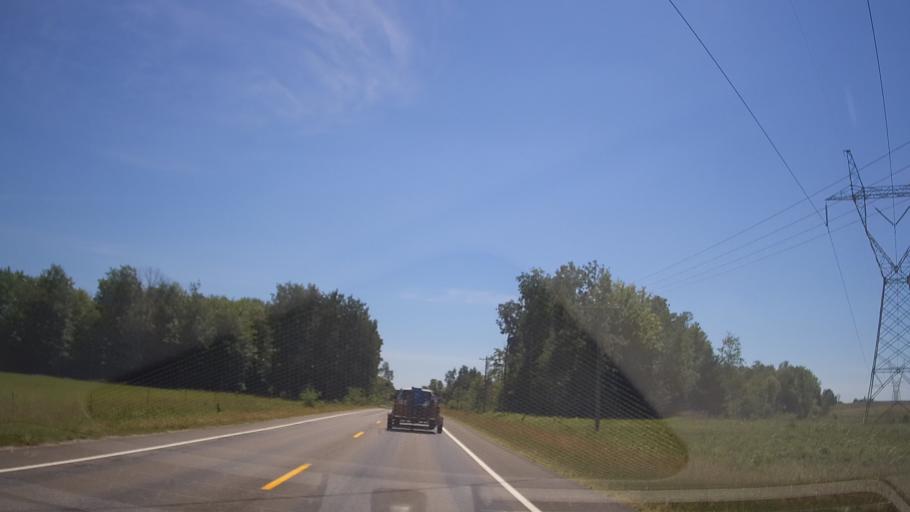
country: US
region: Michigan
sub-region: Grand Traverse County
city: Kingsley
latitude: 44.5951
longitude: -85.6964
